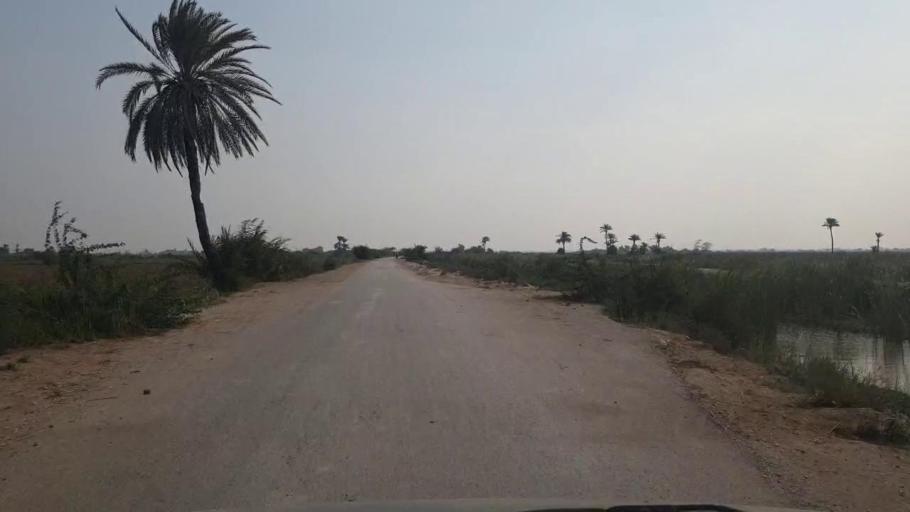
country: PK
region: Sindh
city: Tando Muhammad Khan
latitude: 25.0975
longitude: 68.3786
